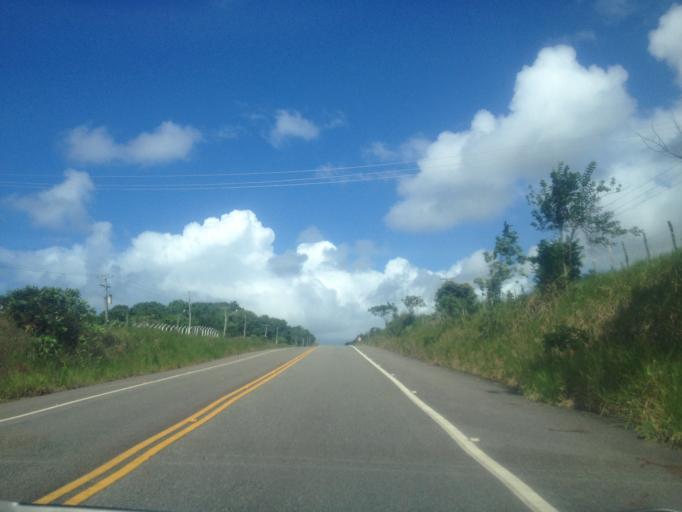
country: BR
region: Sergipe
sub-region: Indiaroba
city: Indiaroba
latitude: -11.4795
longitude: -37.4872
